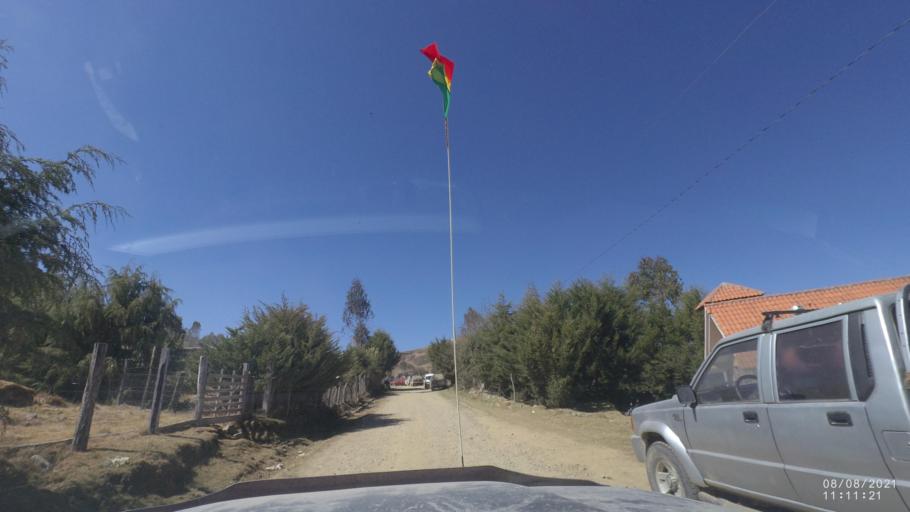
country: BO
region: Cochabamba
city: Colchani
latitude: -16.7618
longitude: -66.6682
